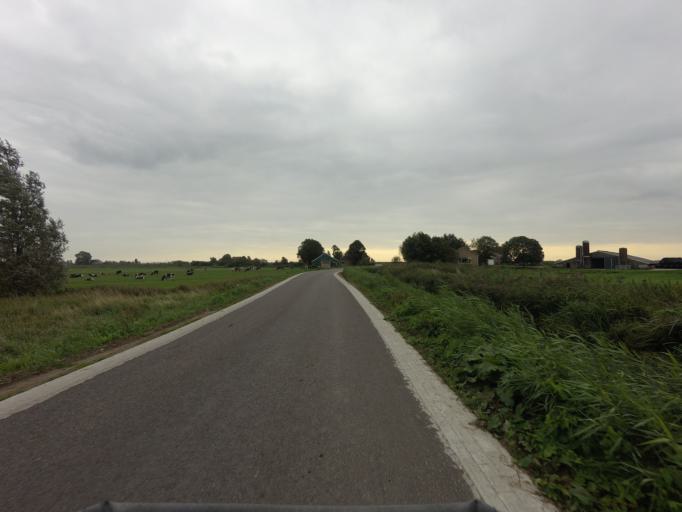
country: NL
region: Friesland
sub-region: Sudwest Fryslan
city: IJlst
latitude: 53.0056
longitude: 5.5930
